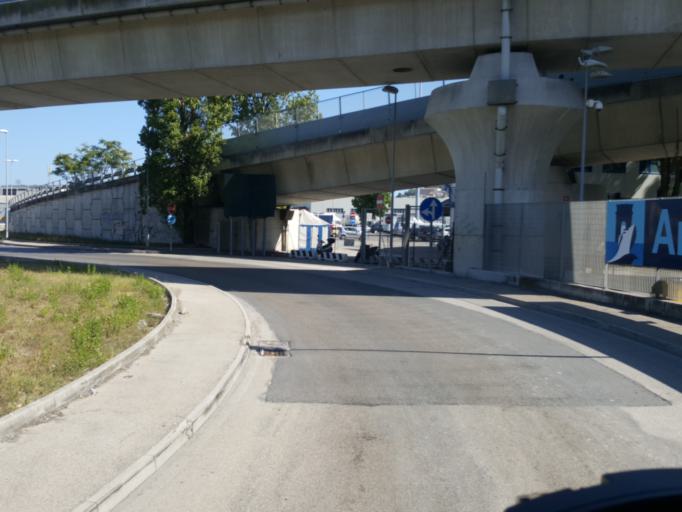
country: IT
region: The Marches
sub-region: Provincia di Ancona
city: Posatora
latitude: 43.6119
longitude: 13.4990
